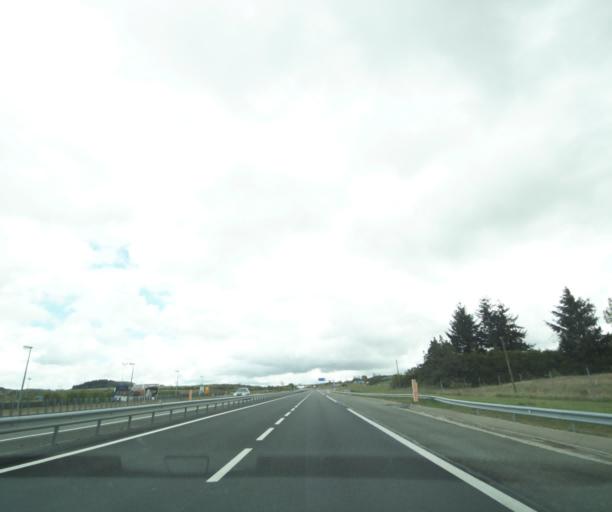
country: FR
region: Midi-Pyrenees
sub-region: Departement de l'Aveyron
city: La Cavalerie
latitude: 43.9847
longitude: 3.1826
